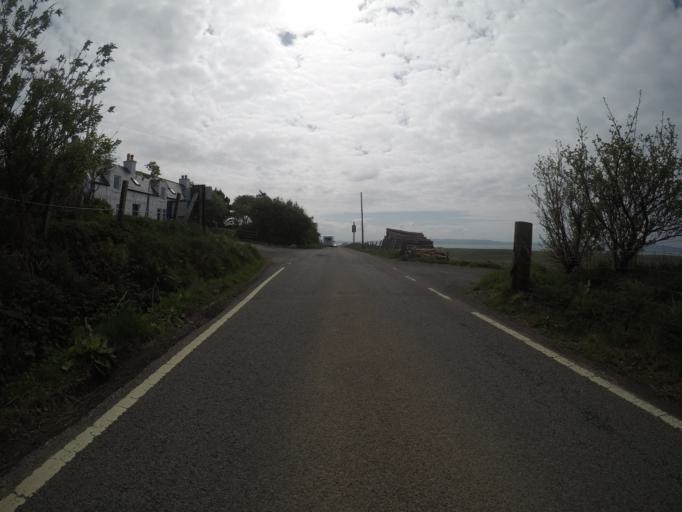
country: GB
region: Scotland
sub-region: Highland
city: Portree
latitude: 57.6329
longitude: -6.3773
